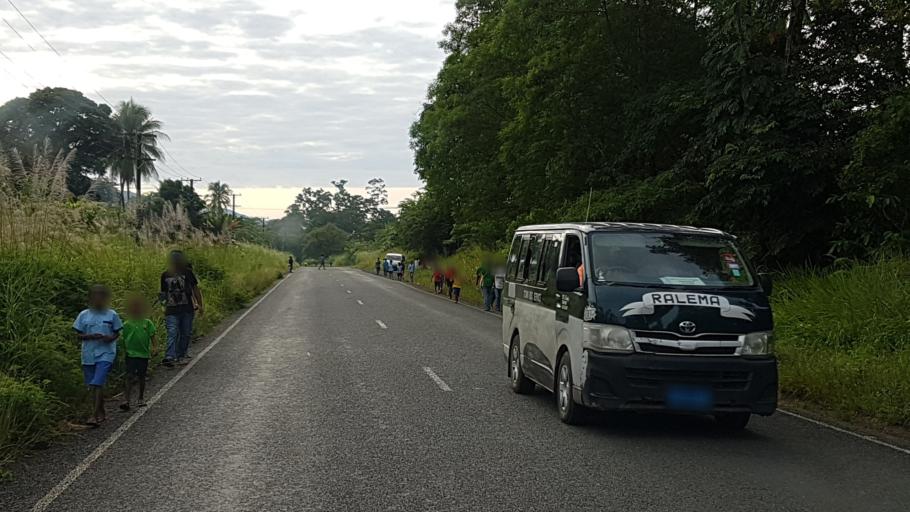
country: PG
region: Milne Bay
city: Alotau
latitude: -10.3159
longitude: 150.4647
